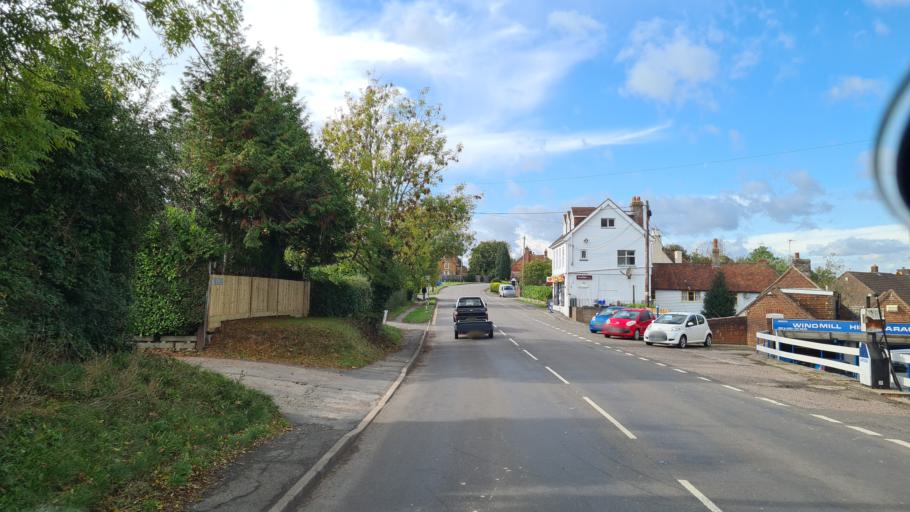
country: GB
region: England
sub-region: East Sussex
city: Bodle Street
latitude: 50.8841
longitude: 0.3453
